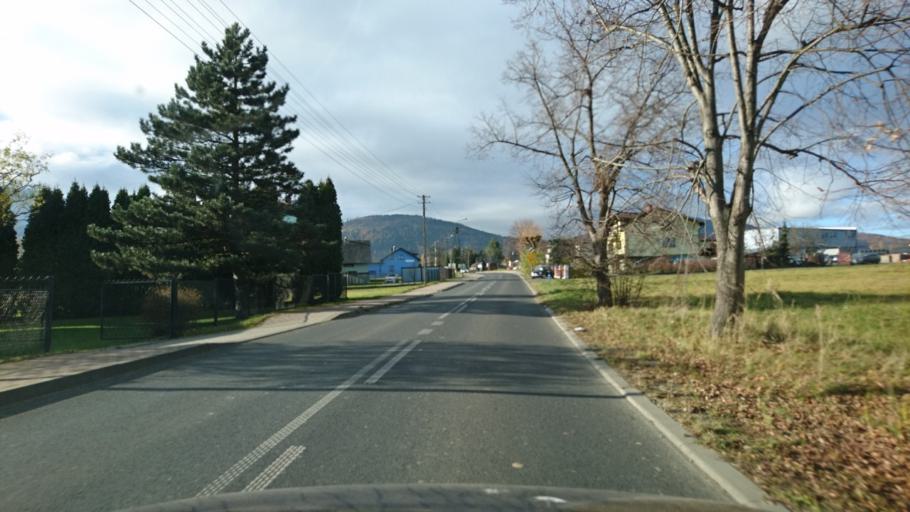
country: PL
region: Silesian Voivodeship
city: Godziszka
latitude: 49.7071
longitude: 19.0929
